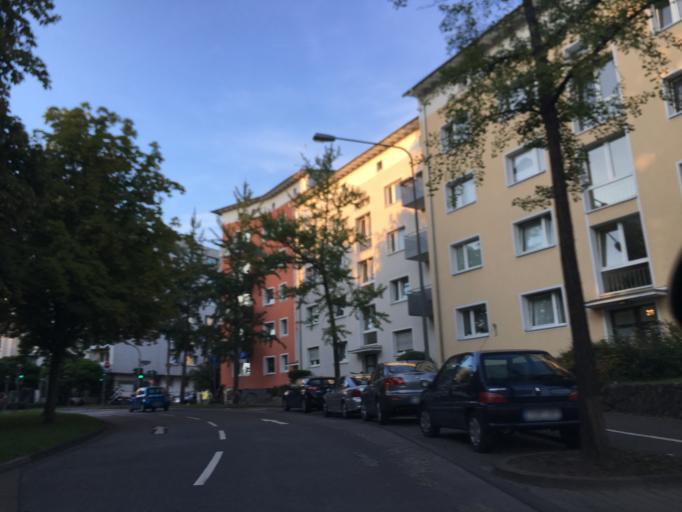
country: DE
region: Hesse
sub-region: Regierungsbezirk Darmstadt
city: Frankfurt am Main
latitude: 50.1153
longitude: 8.7100
